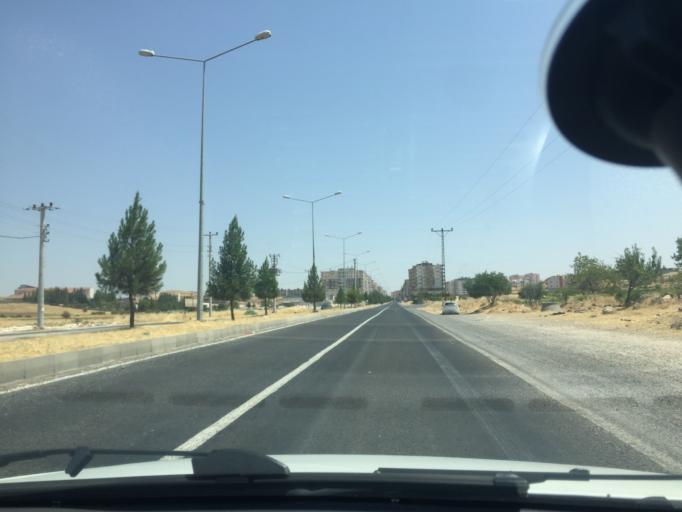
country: TR
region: Mardin
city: Midyat
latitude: 37.4360
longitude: 41.3198
